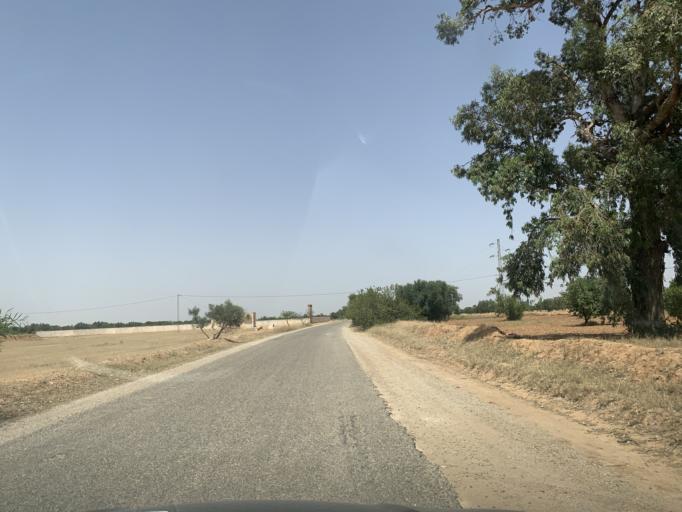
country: TN
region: Al Mahdiyah
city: Shurban
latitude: 35.1811
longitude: 10.2371
